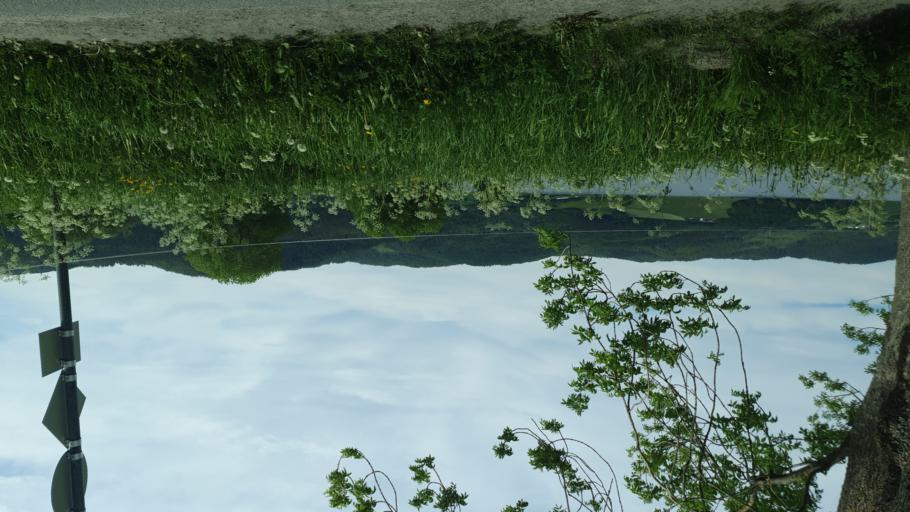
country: NO
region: Sor-Trondelag
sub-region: Rissa
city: Rissa
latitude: 63.5657
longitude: 9.9270
